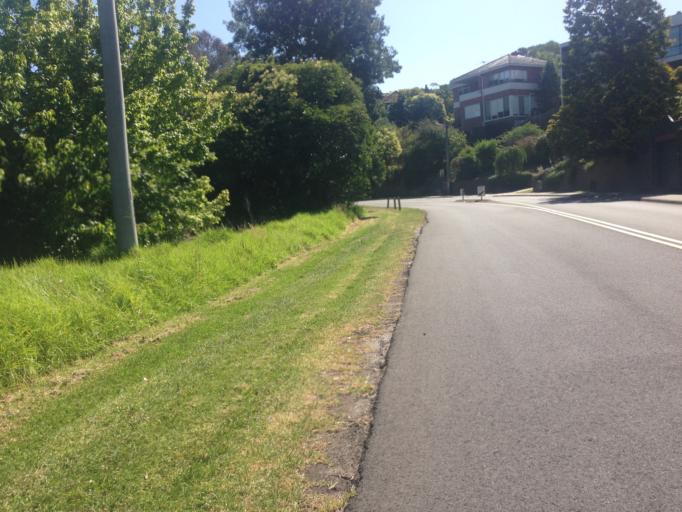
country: AU
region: Victoria
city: Ivanhoe East
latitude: -37.7767
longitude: 145.0466
